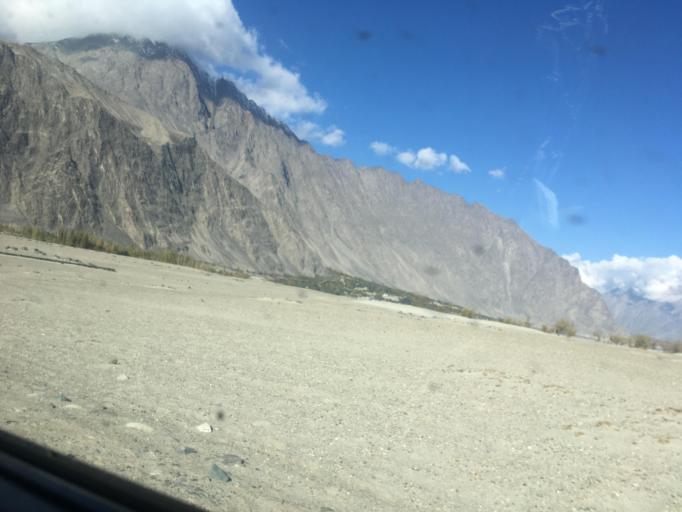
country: PK
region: Gilgit-Baltistan
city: Skardu
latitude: 35.3572
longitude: 75.5267
